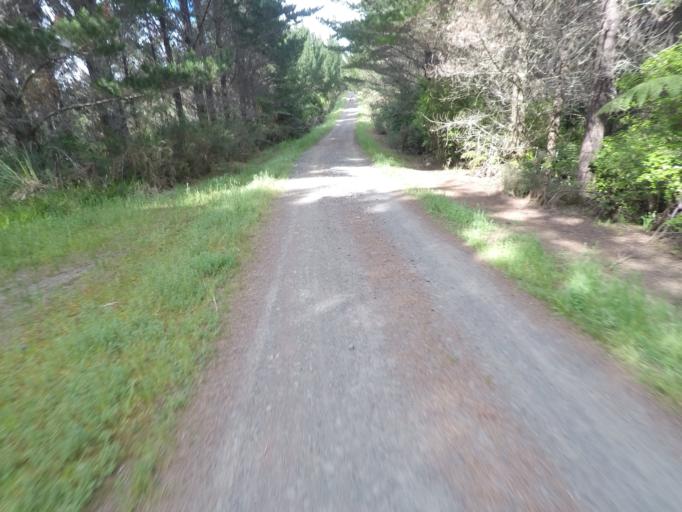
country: NZ
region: Auckland
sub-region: Auckland
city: Muriwai Beach
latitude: -36.7458
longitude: 174.5649
